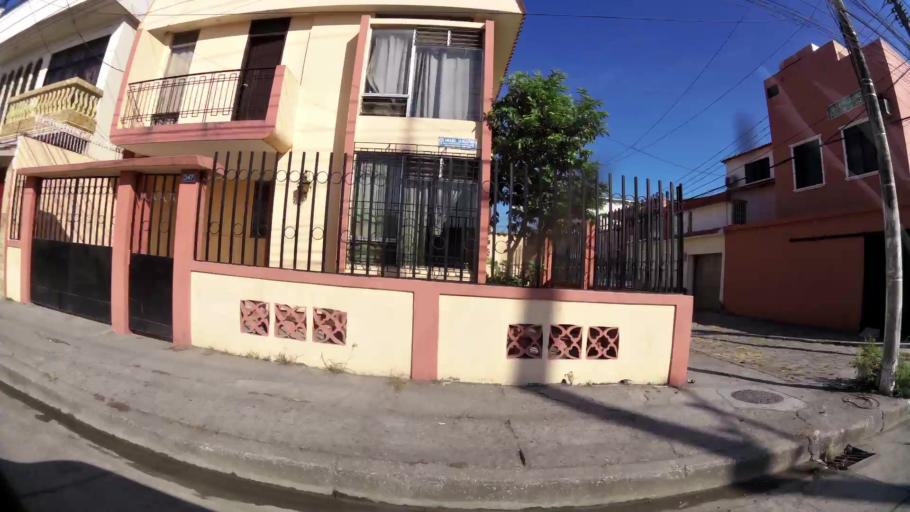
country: EC
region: Guayas
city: Guayaquil
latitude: -2.1740
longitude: -79.8948
